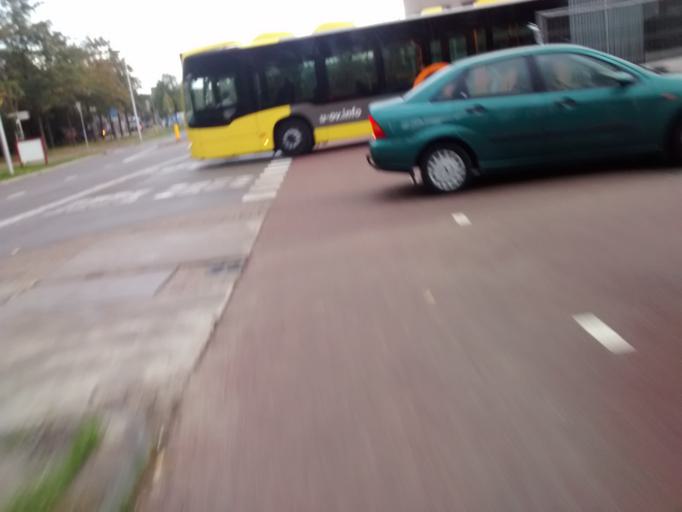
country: NL
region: Utrecht
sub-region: Gemeente Utrecht
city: Lunetten
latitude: 52.0655
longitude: 5.1421
